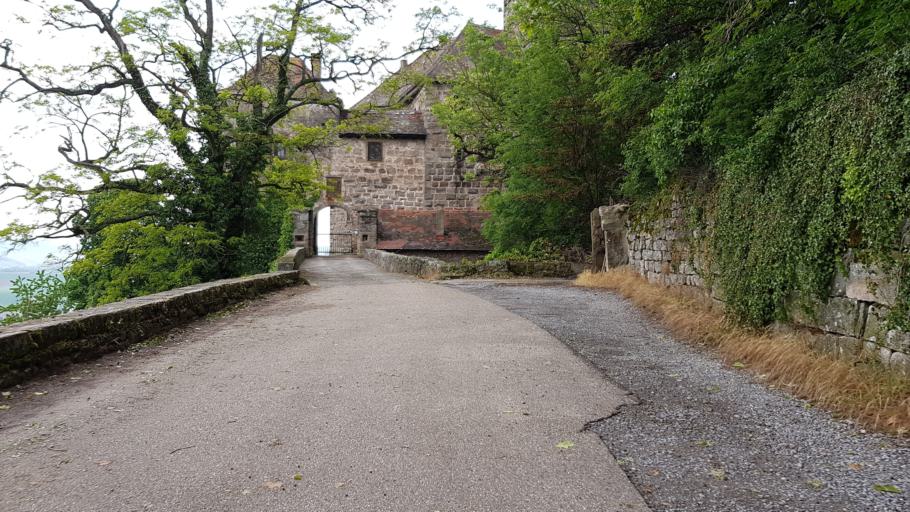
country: DE
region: Baden-Wuerttemberg
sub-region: Regierungsbezirk Stuttgart
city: Oberstenfeld
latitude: 49.0133
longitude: 9.3273
